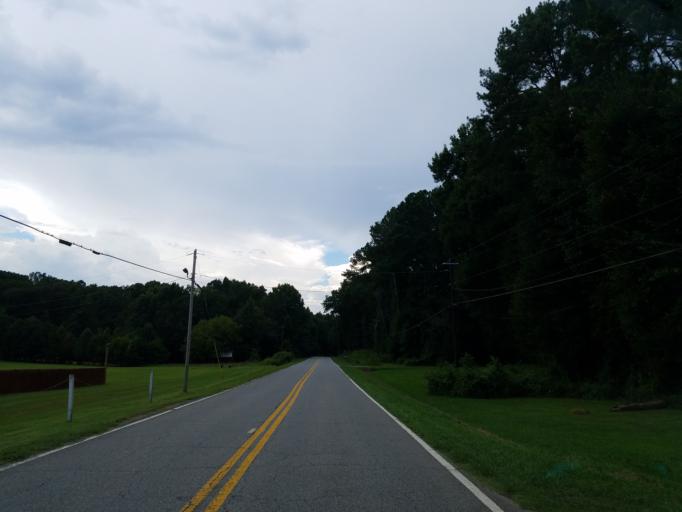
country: US
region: Georgia
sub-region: Bartow County
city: Cartersville
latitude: 34.2555
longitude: -84.8558
